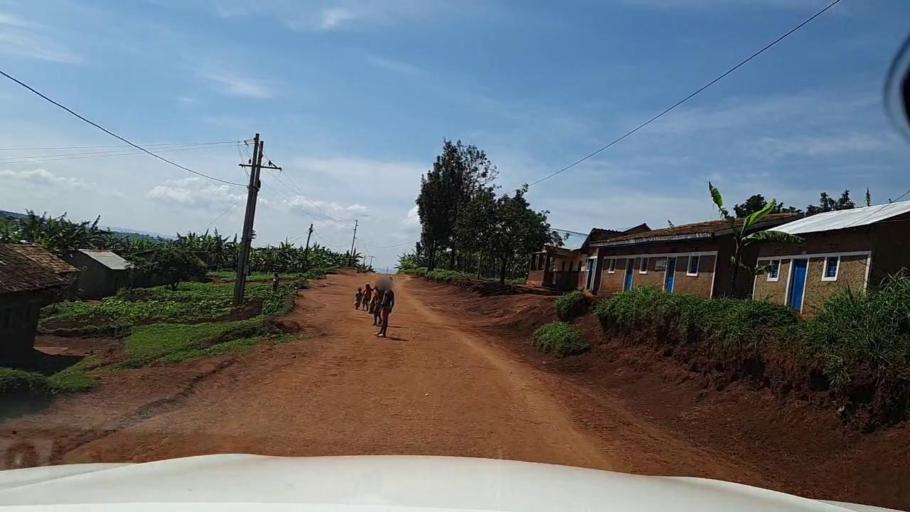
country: RW
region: Southern Province
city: Butare
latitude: -2.7088
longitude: 29.8392
